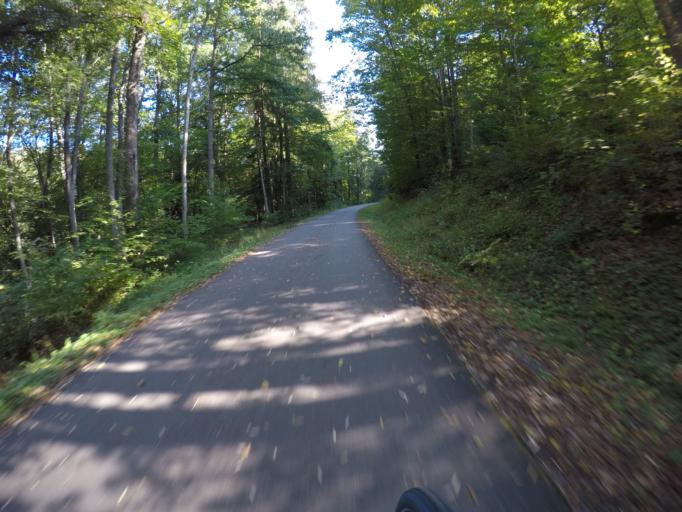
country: DE
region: Baden-Wuerttemberg
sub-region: Regierungsbezirk Stuttgart
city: Waldenbuch
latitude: 48.6548
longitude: 9.1553
